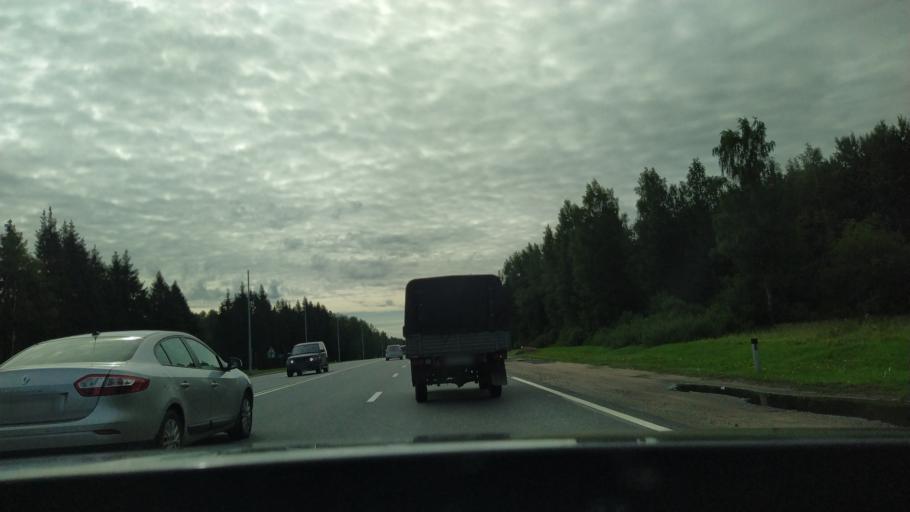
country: RU
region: Leningrad
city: Ul'yanovka
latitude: 59.5905
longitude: 30.7869
